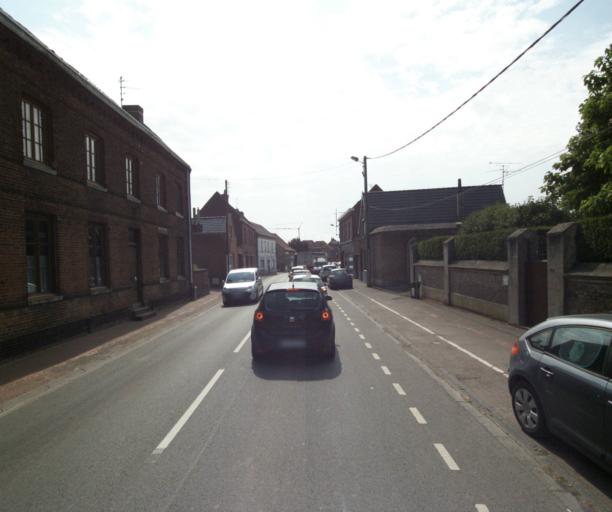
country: FR
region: Nord-Pas-de-Calais
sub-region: Departement du Nord
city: Sainghin-en-Weppes
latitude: 50.5646
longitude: 2.8966
